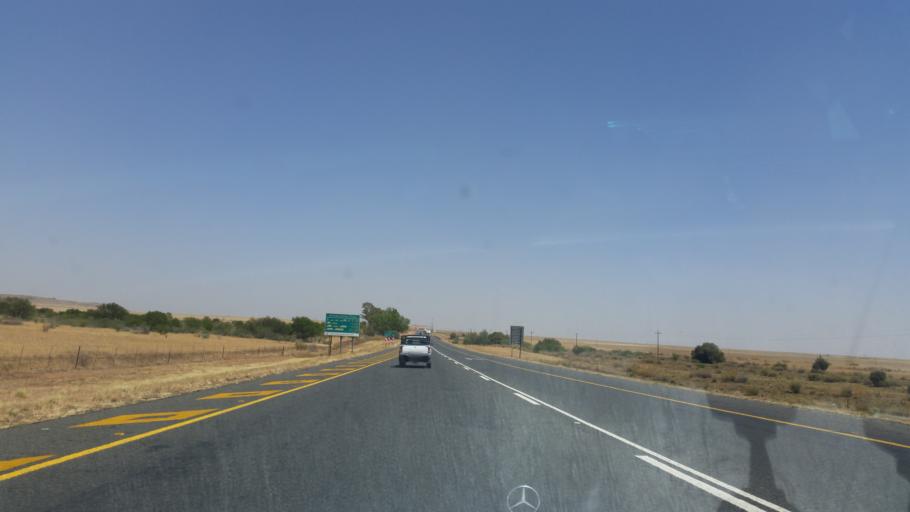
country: ZA
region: Orange Free State
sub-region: Lejweleputswa District Municipality
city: Brandfort
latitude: -28.7895
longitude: 26.7026
